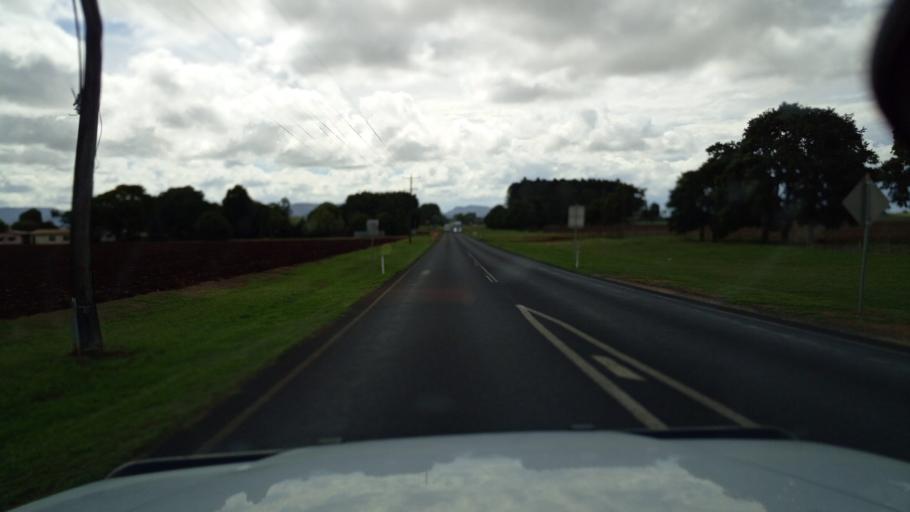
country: AU
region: Queensland
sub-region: Tablelands
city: Tolga
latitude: -17.2160
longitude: 145.5372
